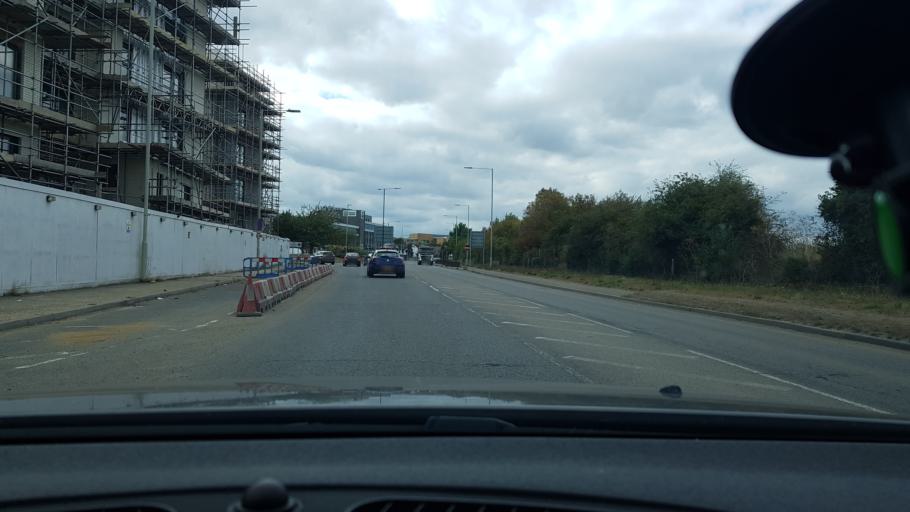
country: GB
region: England
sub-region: Surrey
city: Colnbrook
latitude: 51.4884
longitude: -0.5322
